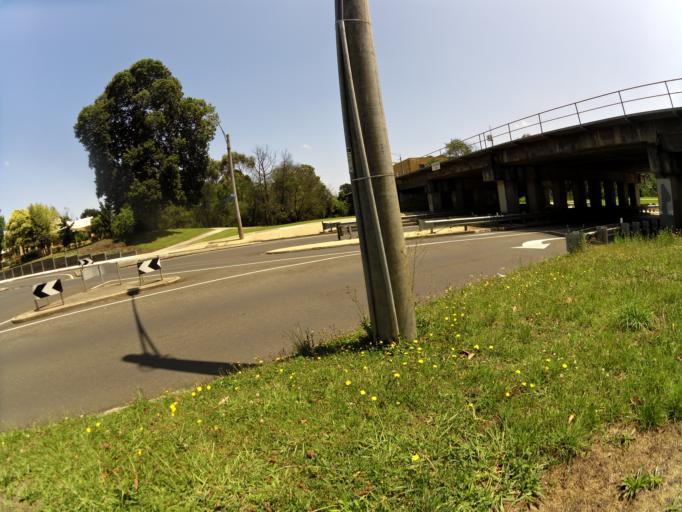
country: AU
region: Victoria
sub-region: Latrobe
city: Traralgon
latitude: -38.1978
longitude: 146.5428
